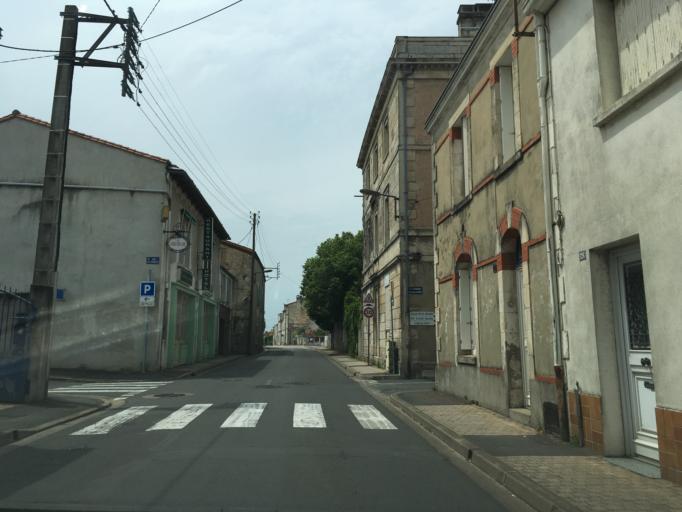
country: FR
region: Poitou-Charentes
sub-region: Departement des Deux-Sevres
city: Niort
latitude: 46.3222
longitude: -0.4756
